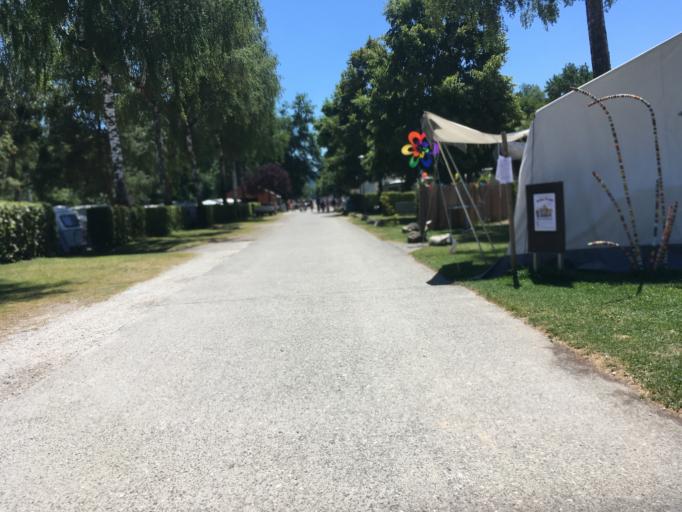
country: CH
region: Vaud
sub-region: Broye-Vully District
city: Avenches
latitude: 46.9045
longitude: 7.0489
